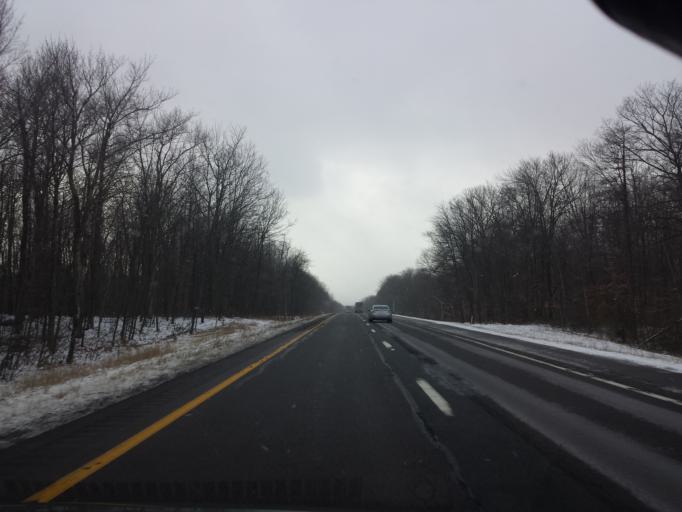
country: US
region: Pennsylvania
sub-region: Luzerne County
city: White Haven
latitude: 41.0777
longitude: -75.6699
